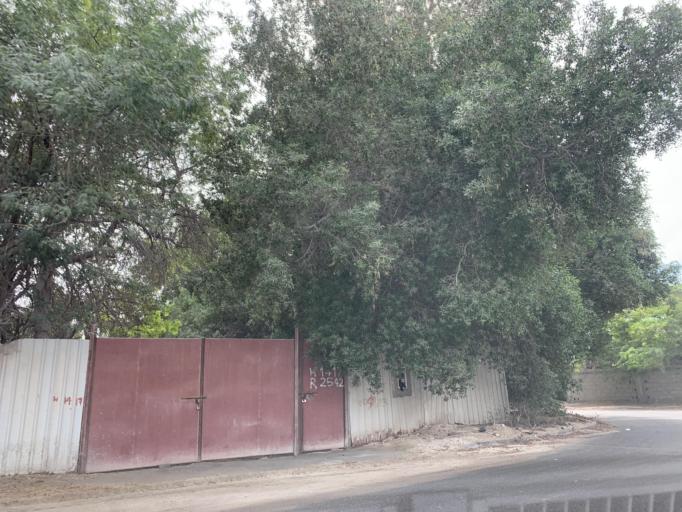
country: BH
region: Central Governorate
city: Madinat Hamad
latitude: 26.1154
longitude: 50.4721
